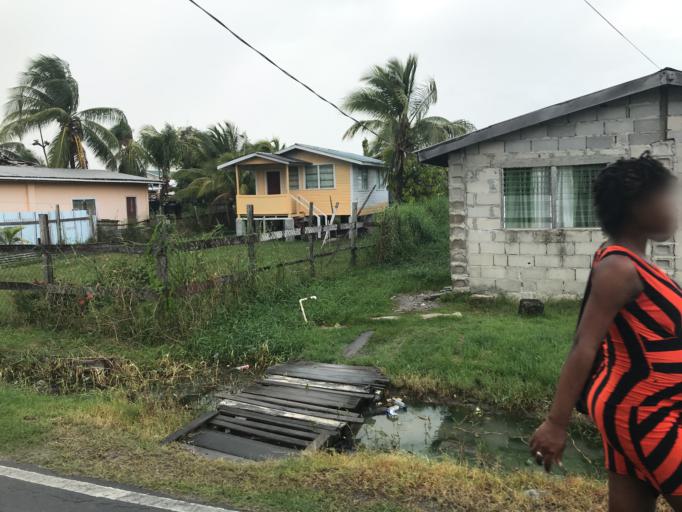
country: GY
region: Demerara-Mahaica
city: Georgetown
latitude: 6.8014
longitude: -58.1195
